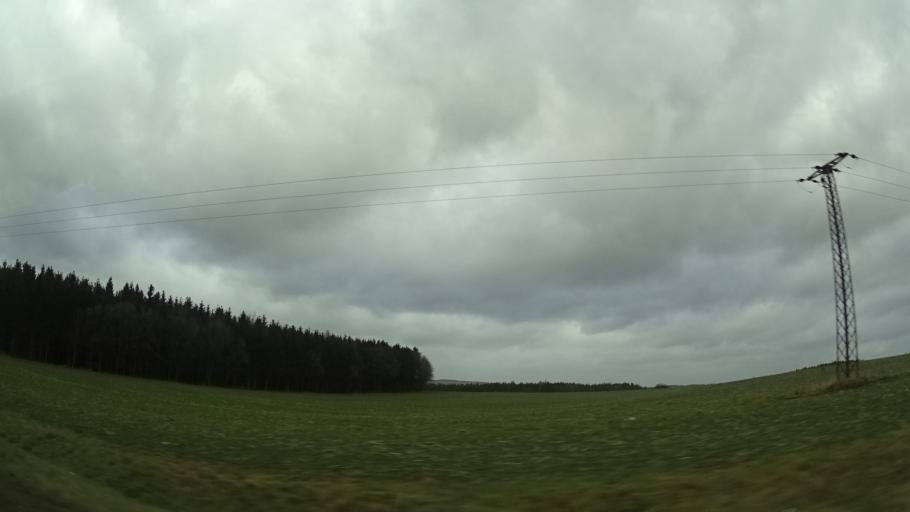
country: DE
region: Thuringia
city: Auma
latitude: 50.6739
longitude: 11.9389
